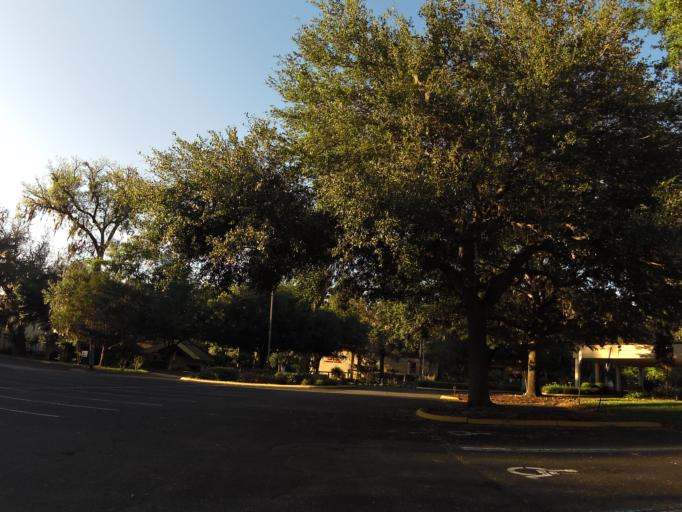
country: US
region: Florida
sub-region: Duval County
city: Atlantic Beach
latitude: 30.3712
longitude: -81.5151
